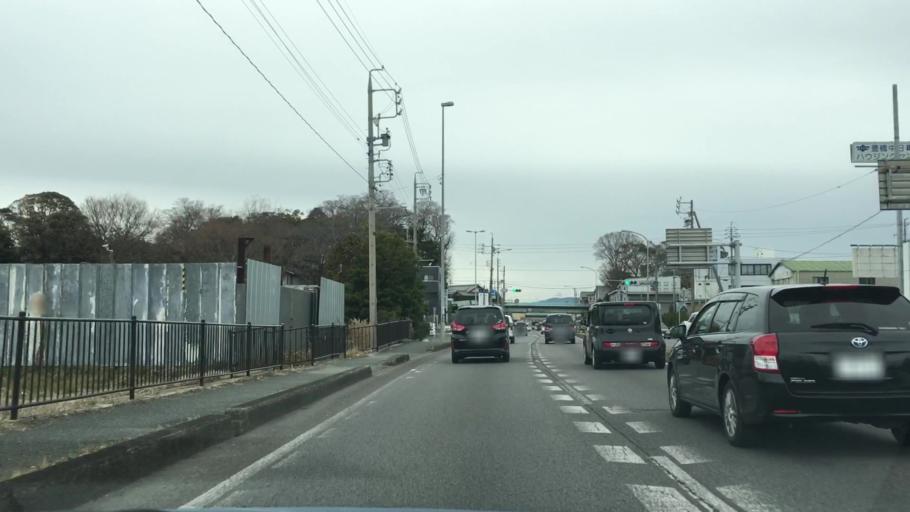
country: JP
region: Aichi
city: Kozakai-cho
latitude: 34.7966
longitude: 137.3676
